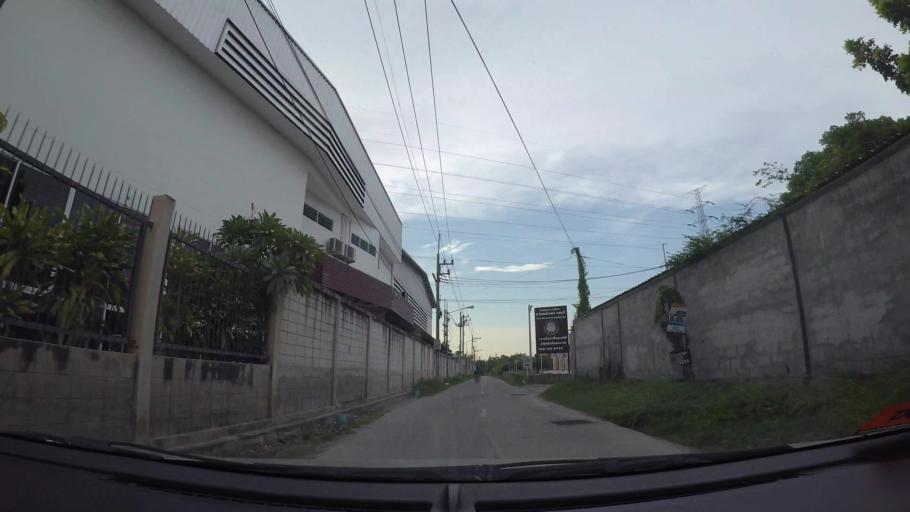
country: TH
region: Chon Buri
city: Chon Buri
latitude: 13.3319
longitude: 100.9855
